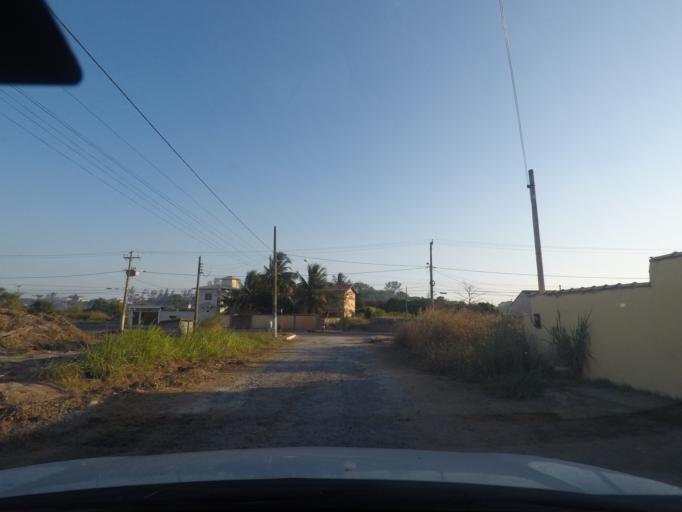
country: BR
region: Rio de Janeiro
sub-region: Marica
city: Marica
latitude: -22.9705
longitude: -42.9280
